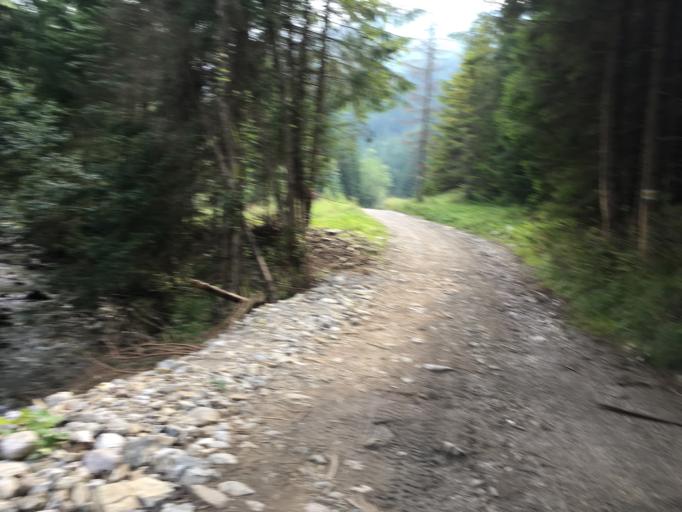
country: PL
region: Lesser Poland Voivodeship
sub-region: Powiat tatrzanski
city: Koscielisko
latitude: 49.2717
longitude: 19.8443
